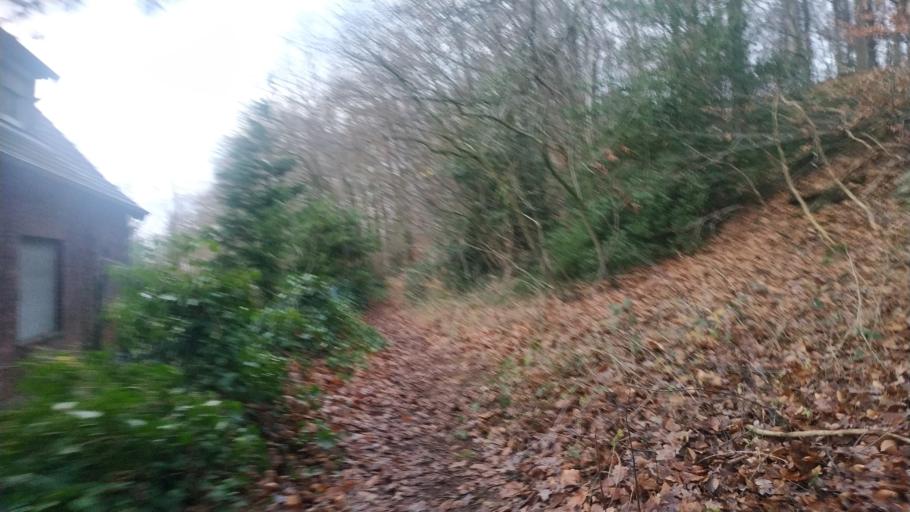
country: DE
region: North Rhine-Westphalia
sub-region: Regierungsbezirk Munster
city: Horstel
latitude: 52.2819
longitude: 7.5902
